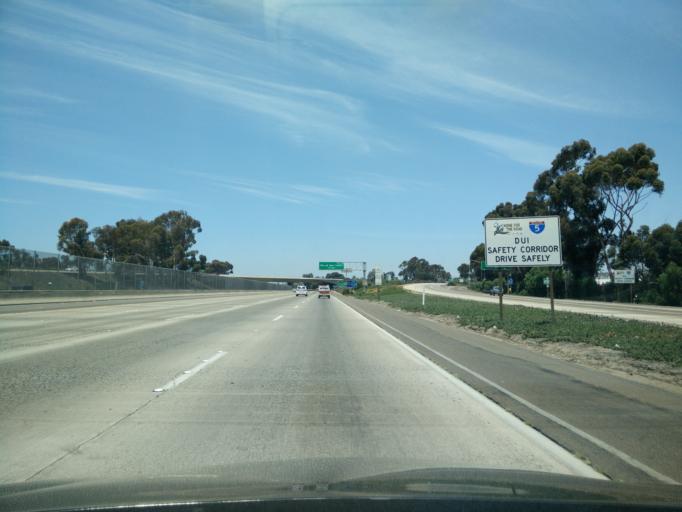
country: MX
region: Baja California
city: Tijuana
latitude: 32.5476
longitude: -117.0371
